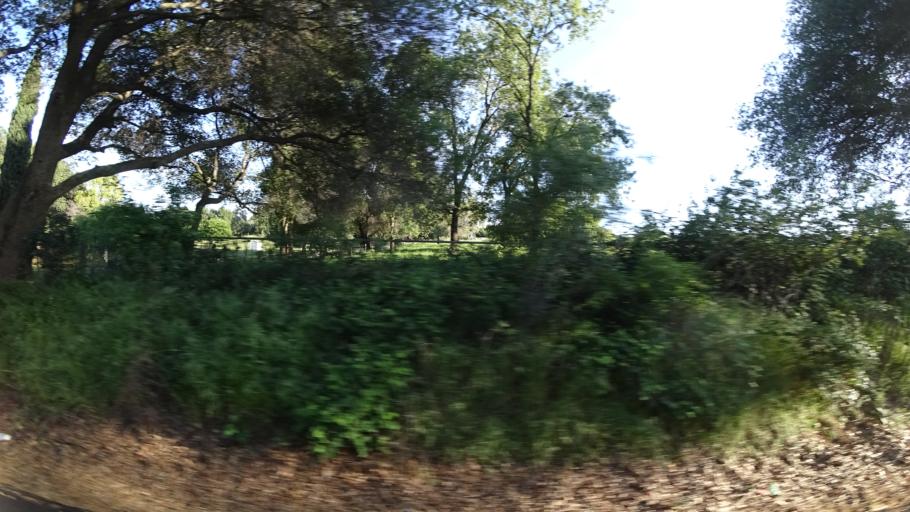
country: US
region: California
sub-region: Placer County
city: Newcastle
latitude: 38.9122
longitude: -121.1916
